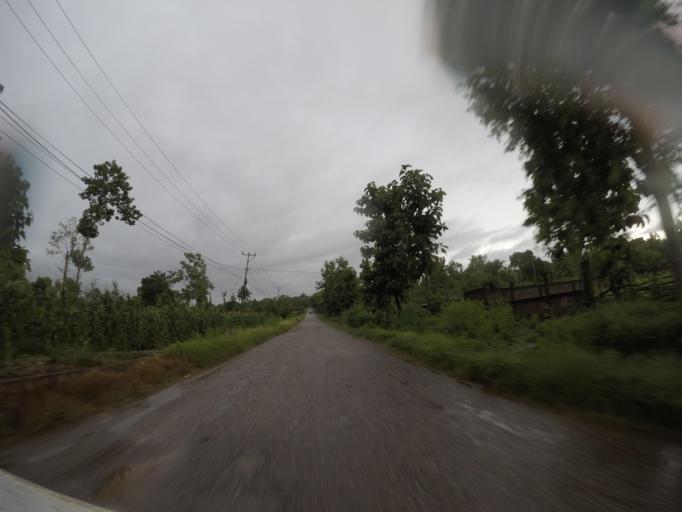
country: TL
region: Bobonaro
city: Maliana
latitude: -8.9622
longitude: 125.1209
